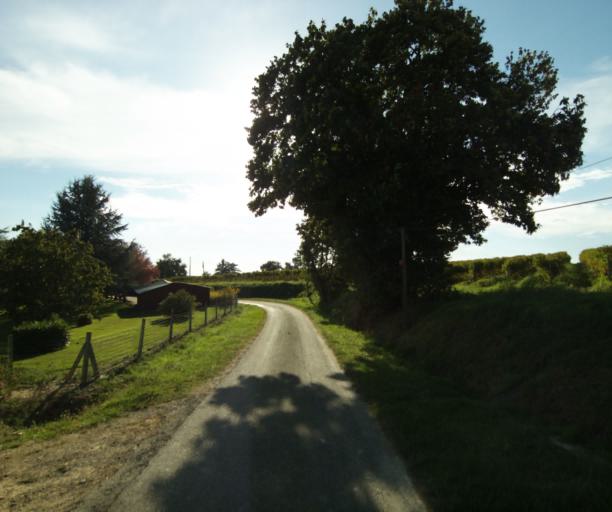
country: FR
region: Midi-Pyrenees
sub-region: Departement du Gers
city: Eauze
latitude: 43.8654
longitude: 0.0440
